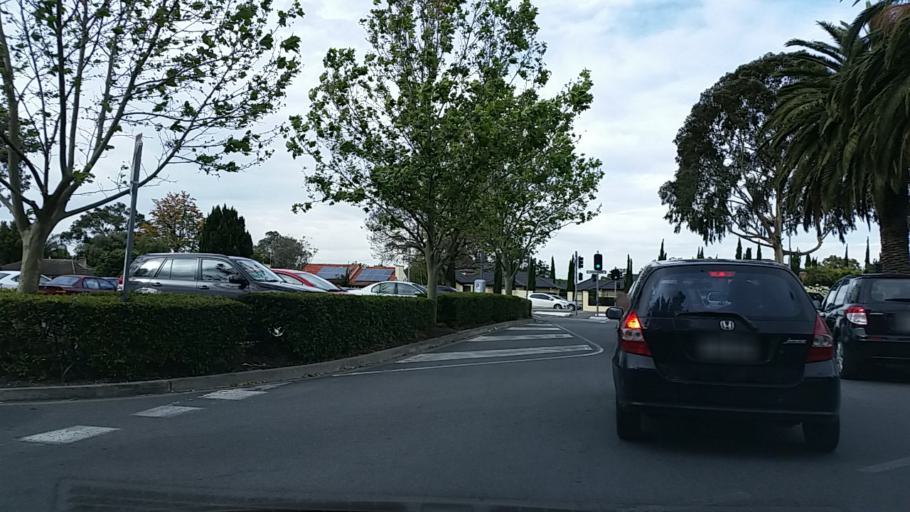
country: AU
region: South Australia
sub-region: Marion
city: Sturt
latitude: -35.0145
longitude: 138.5445
